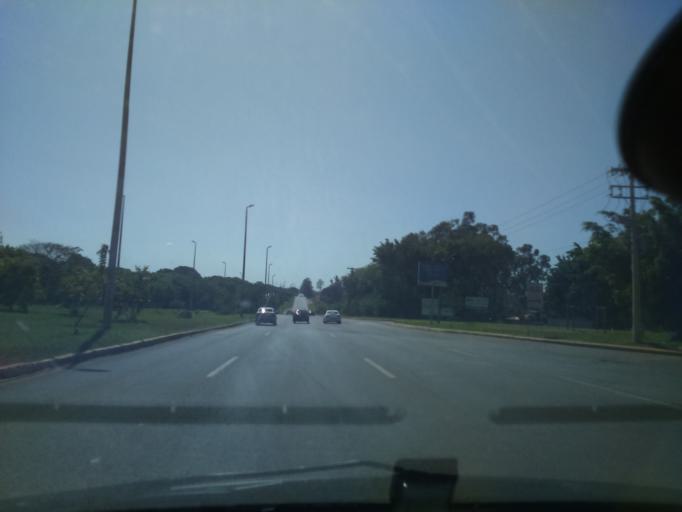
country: BR
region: Federal District
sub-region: Brasilia
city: Brasilia
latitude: -15.8410
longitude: -47.9114
